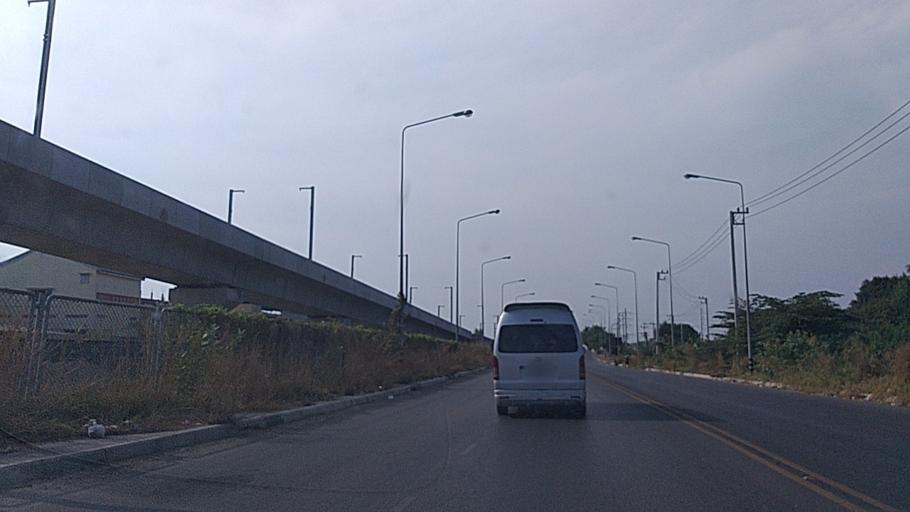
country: TH
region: Phra Nakhon Si Ayutthaya
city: Ban Bang Kadi Pathum Thani
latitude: 13.9830
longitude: 100.6029
